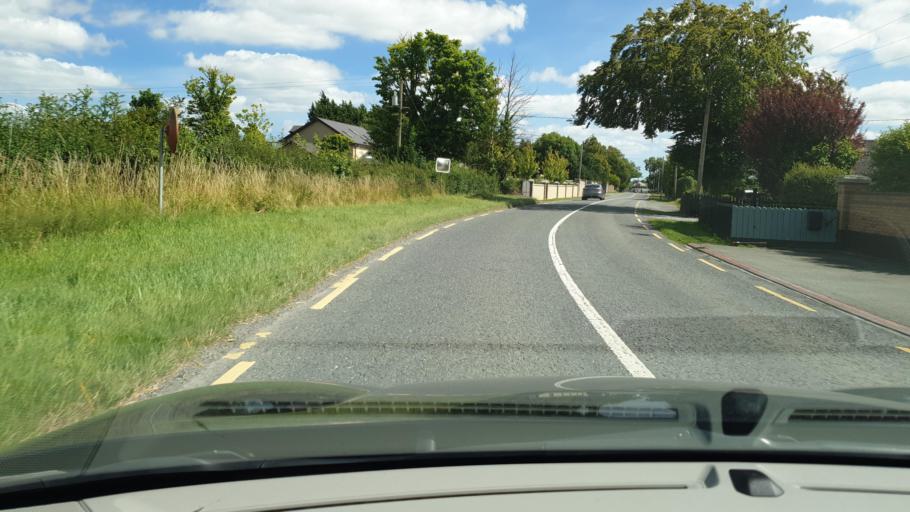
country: IE
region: Leinster
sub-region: An Mhi
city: Dunboyne
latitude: 53.4284
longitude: -6.4995
